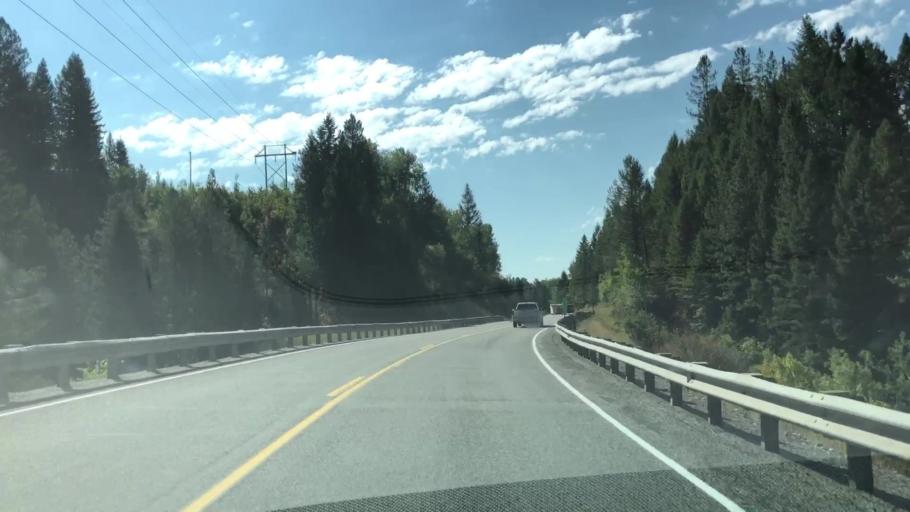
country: US
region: Idaho
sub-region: Teton County
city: Victor
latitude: 43.2996
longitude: -111.1295
